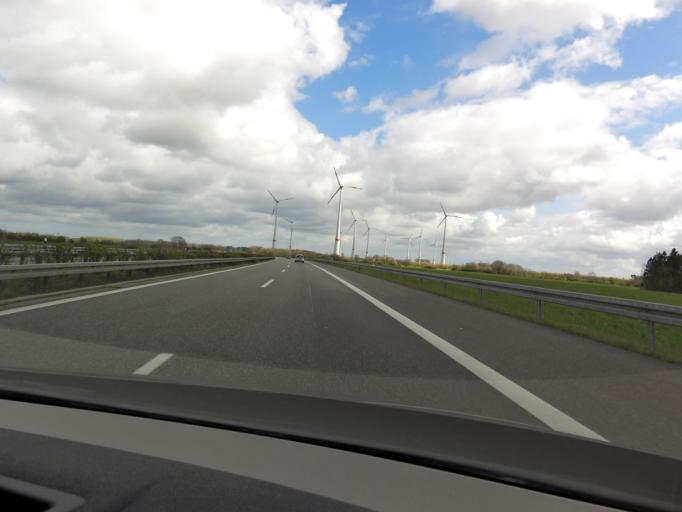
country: DE
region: Mecklenburg-Vorpommern
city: Grimmen
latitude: 54.0802
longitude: 13.0162
